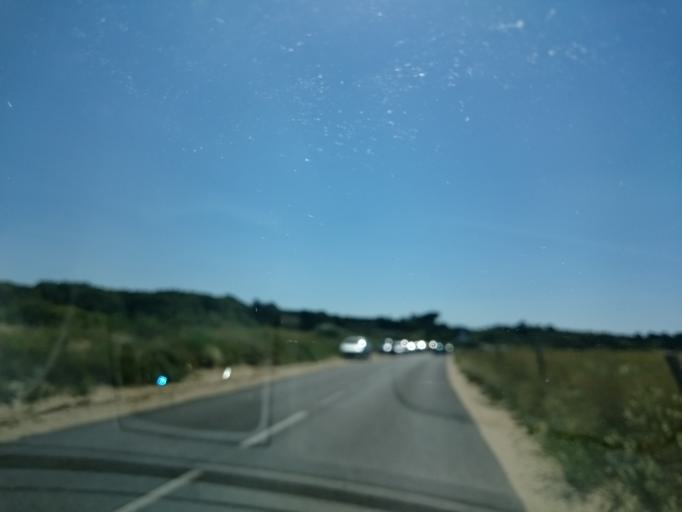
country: FR
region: Brittany
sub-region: Departement d'Ille-et-Vilaine
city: Saint-Coulomb
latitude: 48.6910
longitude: -1.8994
